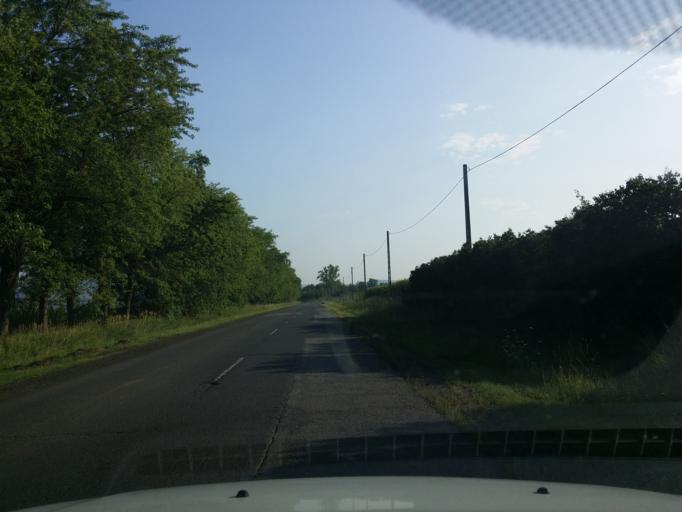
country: HU
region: Borsod-Abauj-Zemplen
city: Abaujszanto
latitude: 48.3396
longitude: 21.2068
